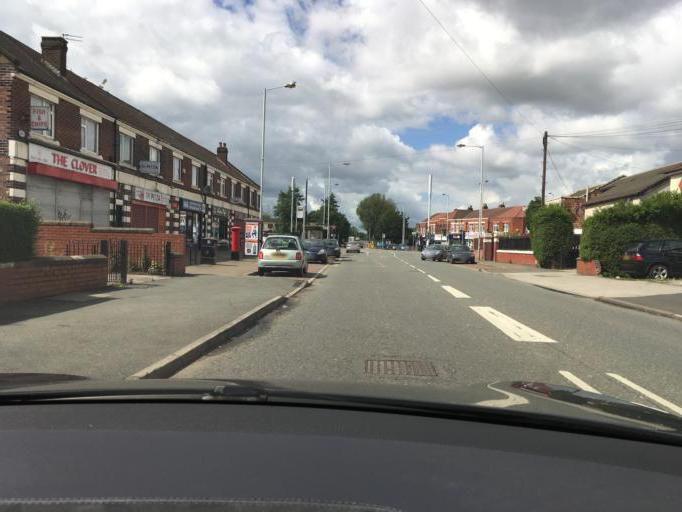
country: GB
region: England
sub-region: Borough of Stockport
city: Stockport
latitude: 53.3889
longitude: -2.1680
